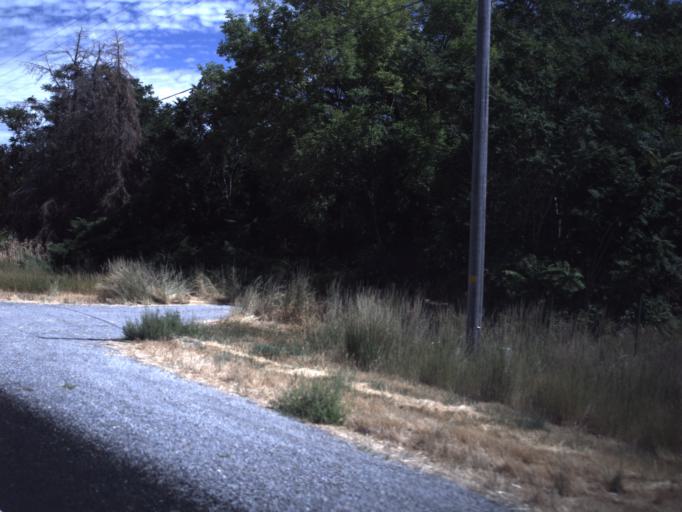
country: US
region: Utah
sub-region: Box Elder County
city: Garland
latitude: 41.7612
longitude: -112.1486
